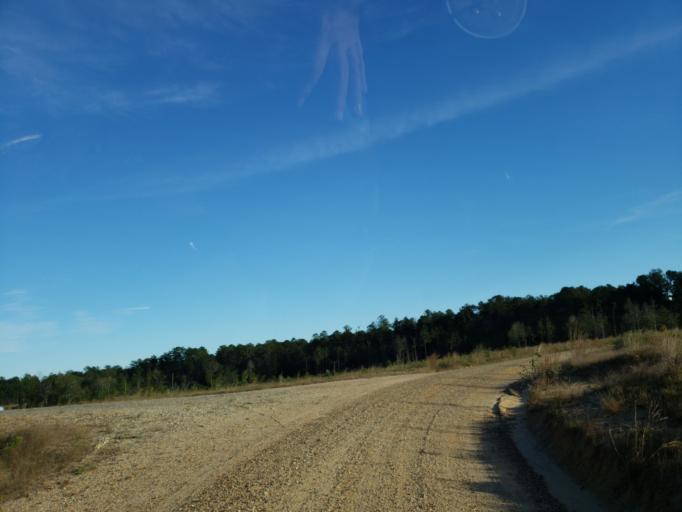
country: US
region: Mississippi
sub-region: Perry County
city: Richton
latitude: 31.3452
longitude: -88.7988
